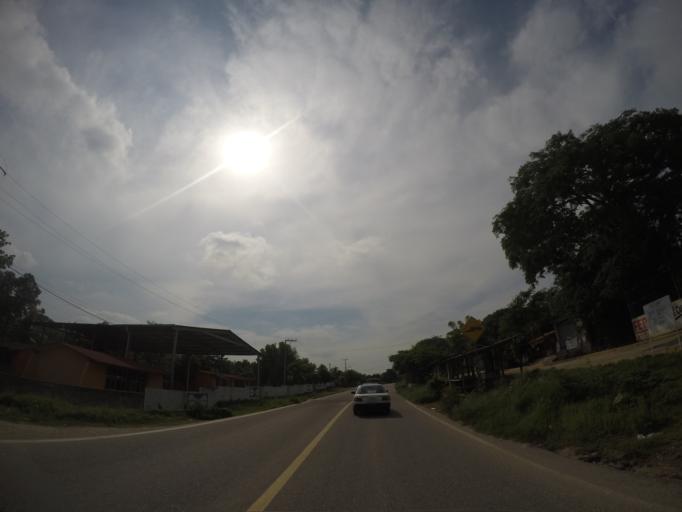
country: MX
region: Guerrero
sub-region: Acapulco de Juarez
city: Cerro de Piedra
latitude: 16.7755
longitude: -99.6289
